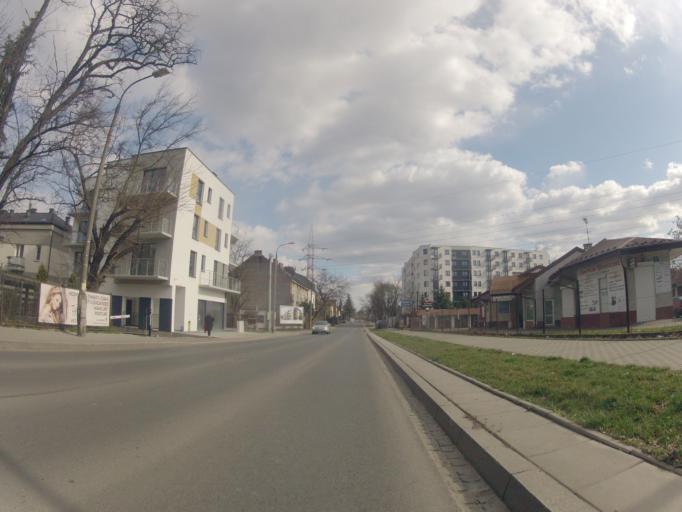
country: PL
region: Lesser Poland Voivodeship
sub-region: Krakow
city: Krakow
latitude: 50.0808
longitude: 19.9567
